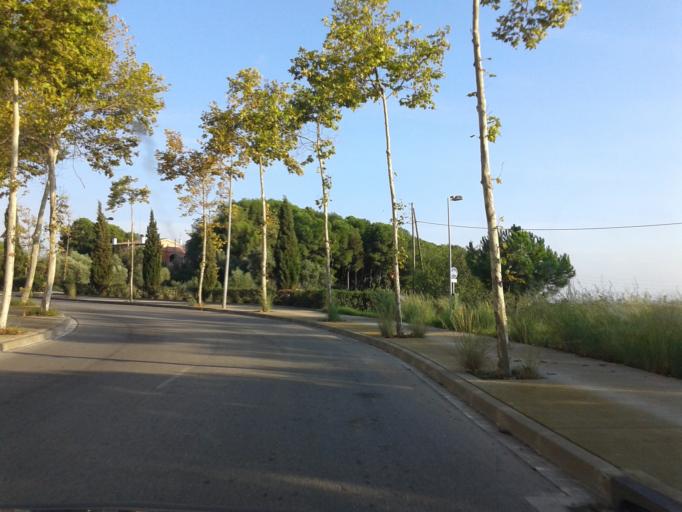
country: ES
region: Catalonia
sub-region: Provincia de Barcelona
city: Vilanova i la Geltru
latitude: 41.2421
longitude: 1.7229
